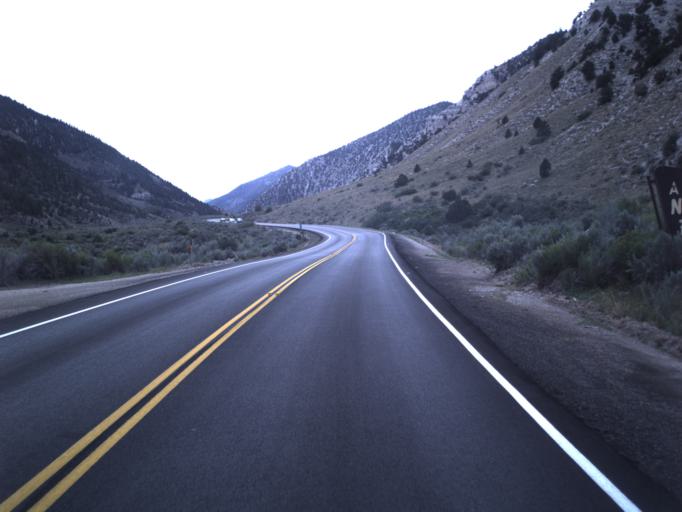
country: US
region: Utah
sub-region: Duchesne County
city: Duchesne
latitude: 39.9959
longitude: -110.5876
